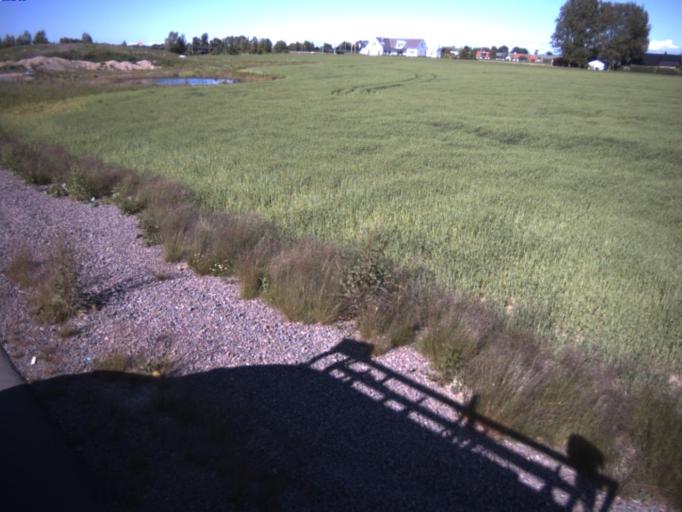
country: SE
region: Skane
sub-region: Helsingborg
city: Rydeback
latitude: 55.9609
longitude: 12.7813
